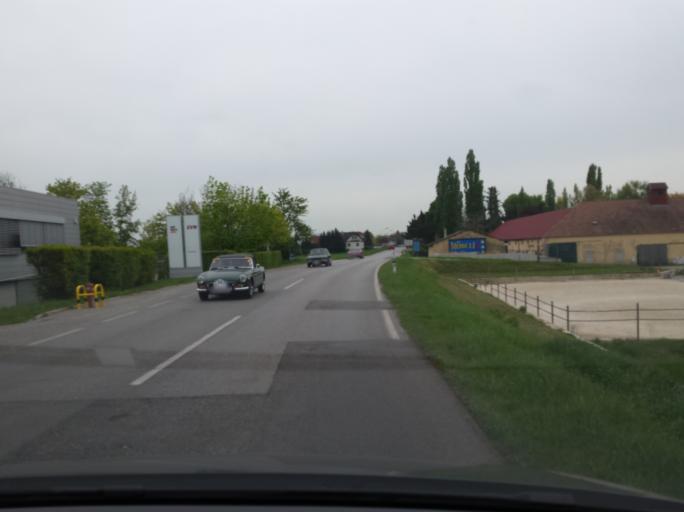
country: AT
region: Lower Austria
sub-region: Politischer Bezirk Bruck an der Leitha
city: Bruck an der Leitha
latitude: 48.0334
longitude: 16.7674
